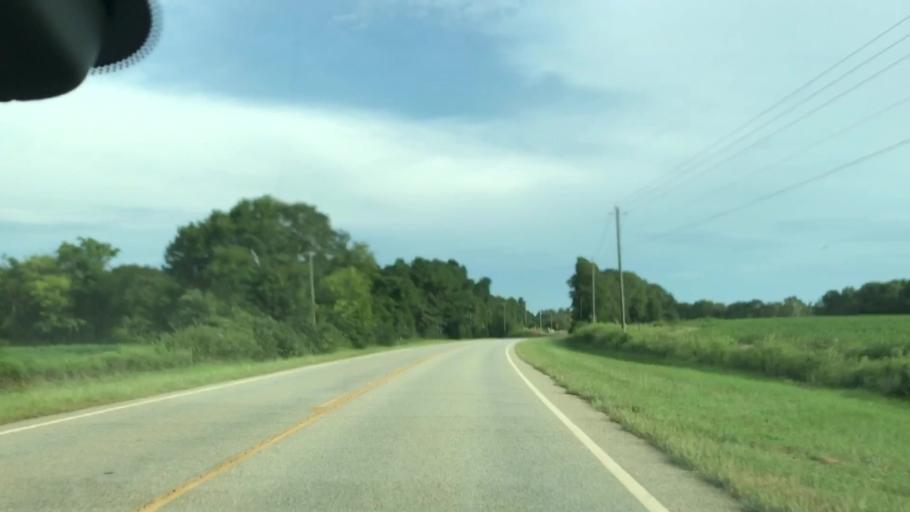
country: US
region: Georgia
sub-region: Clay County
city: Fort Gaines
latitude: 31.7419
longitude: -85.0524
